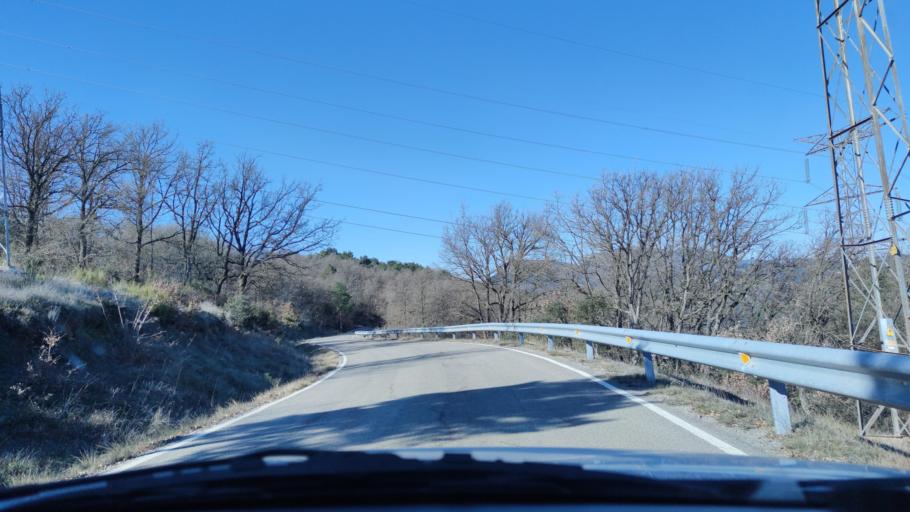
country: ES
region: Catalonia
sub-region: Provincia de Lleida
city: Artesa de Segre
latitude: 42.0527
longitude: 1.0817
